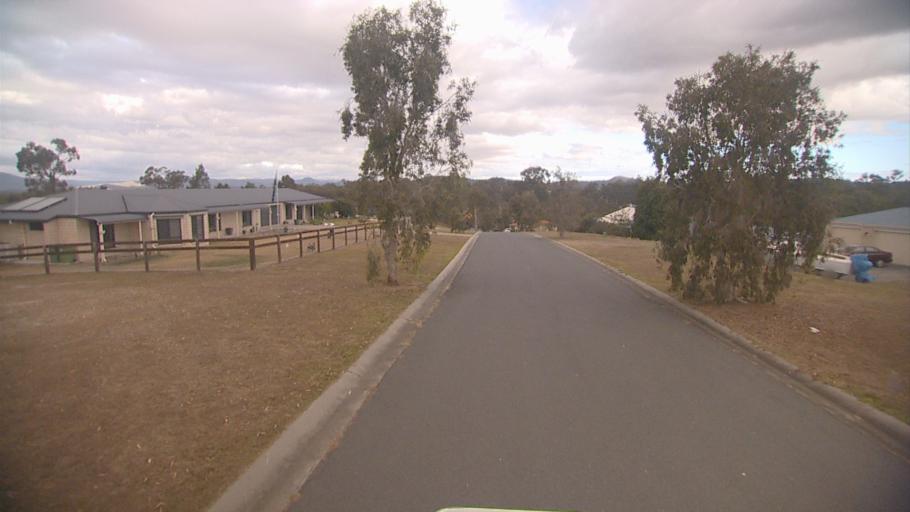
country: AU
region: Queensland
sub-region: Logan
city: Cedar Vale
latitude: -27.8695
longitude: 153.0788
